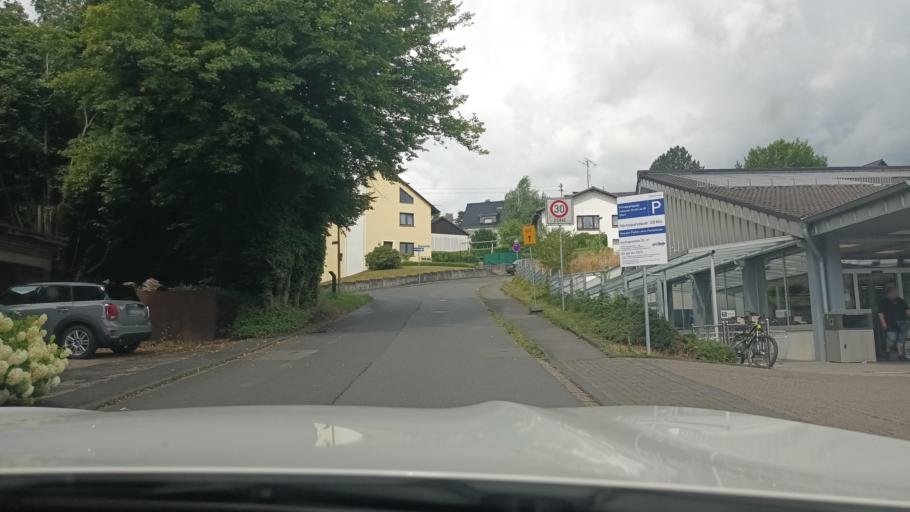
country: DE
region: North Rhine-Westphalia
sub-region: Regierungsbezirk Koln
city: Eitorf
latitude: 50.7661
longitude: 7.4469
